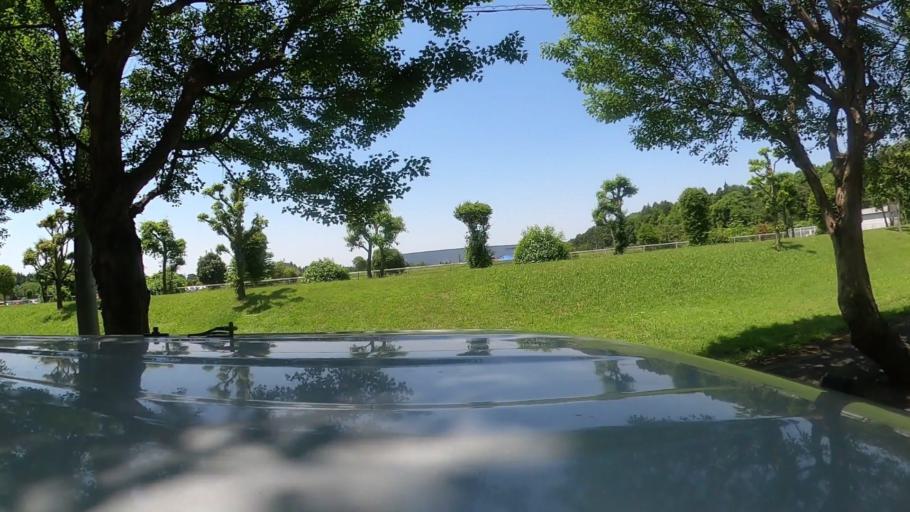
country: JP
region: Ibaraki
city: Ushiku
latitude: 36.0197
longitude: 140.1186
